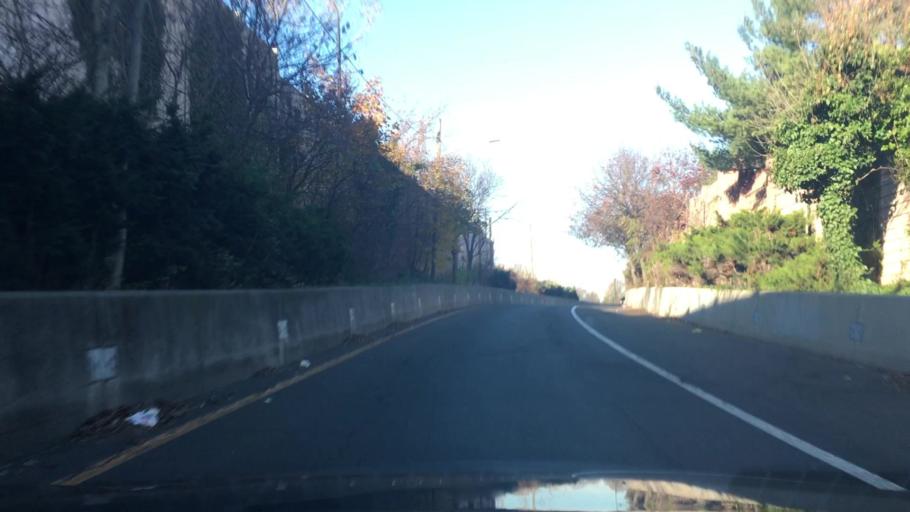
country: US
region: New York
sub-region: Nassau County
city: Plainview
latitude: 40.7997
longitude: -73.4850
